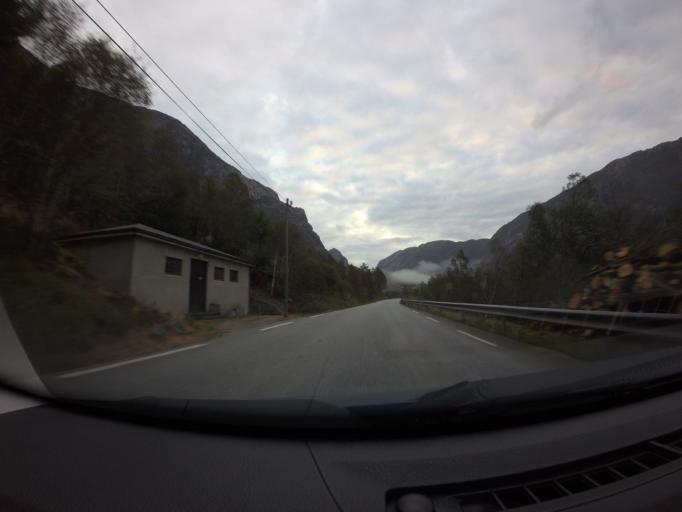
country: NO
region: Rogaland
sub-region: Forsand
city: Forsand
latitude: 58.8364
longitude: 6.0714
